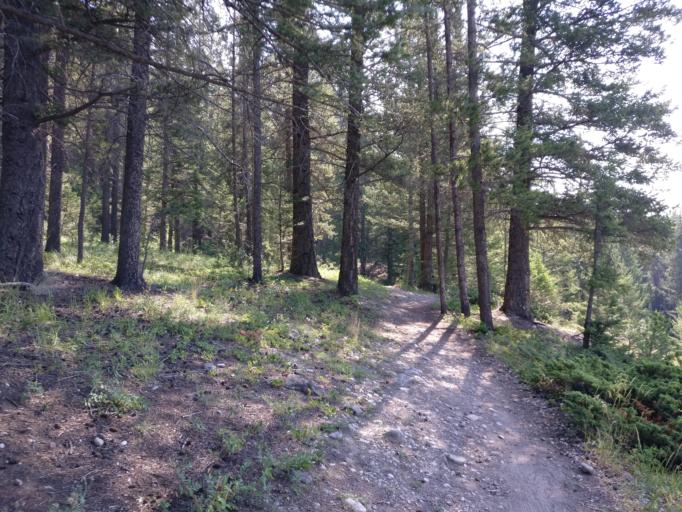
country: CA
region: Alberta
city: Canmore
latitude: 51.0850
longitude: -115.3218
